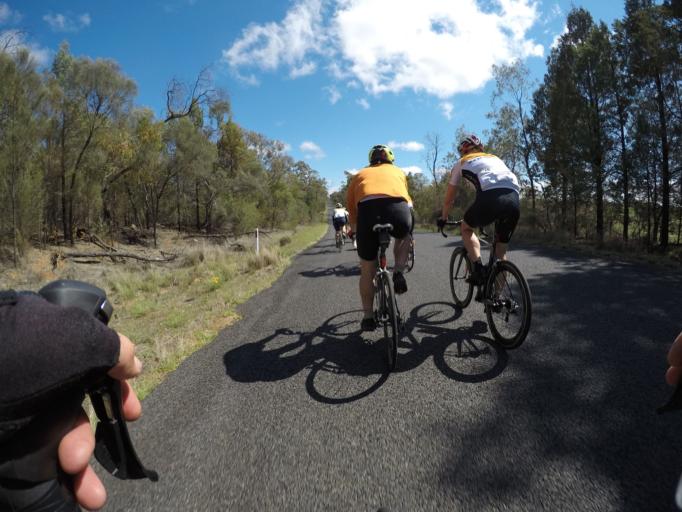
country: AU
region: New South Wales
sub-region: Dubbo Municipality
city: Eulomogo
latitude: -32.6079
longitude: 148.5478
